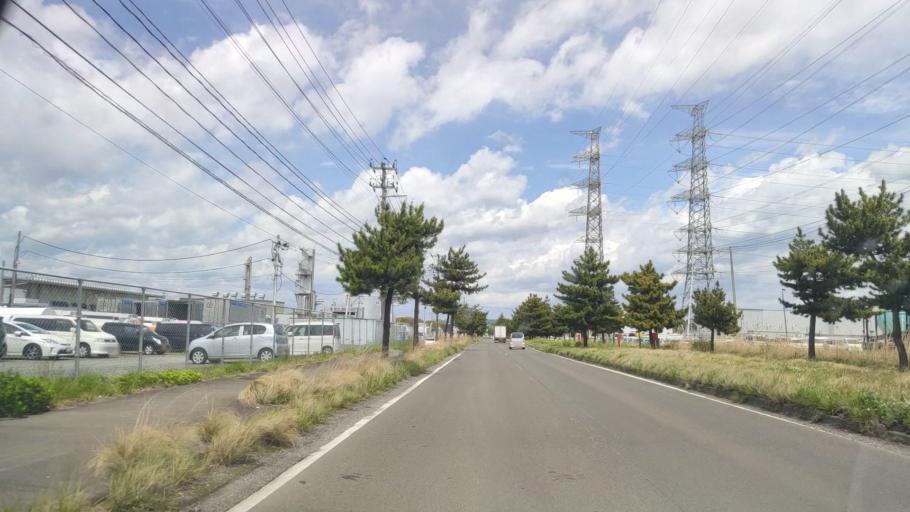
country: JP
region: Miyagi
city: Shiogama
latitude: 38.2842
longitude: 141.0246
